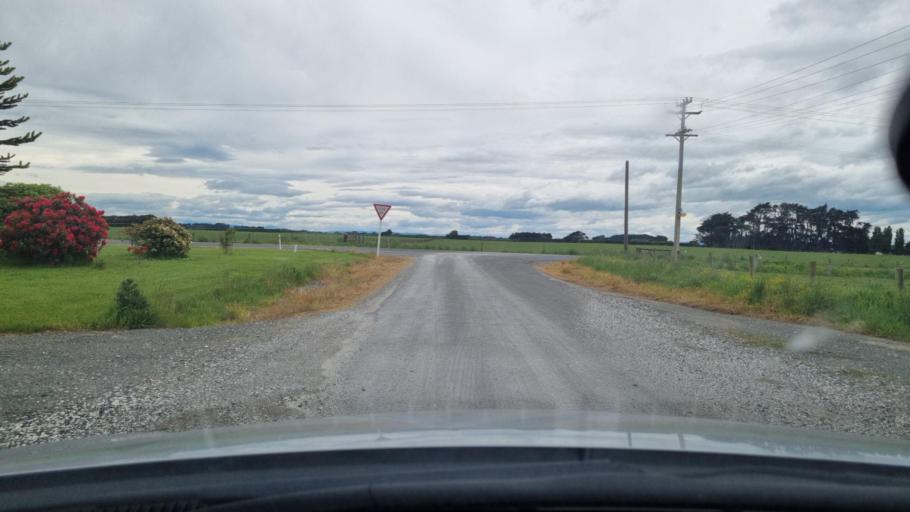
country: NZ
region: Southland
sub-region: Invercargill City
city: Invercargill
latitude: -46.3698
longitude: 168.2984
